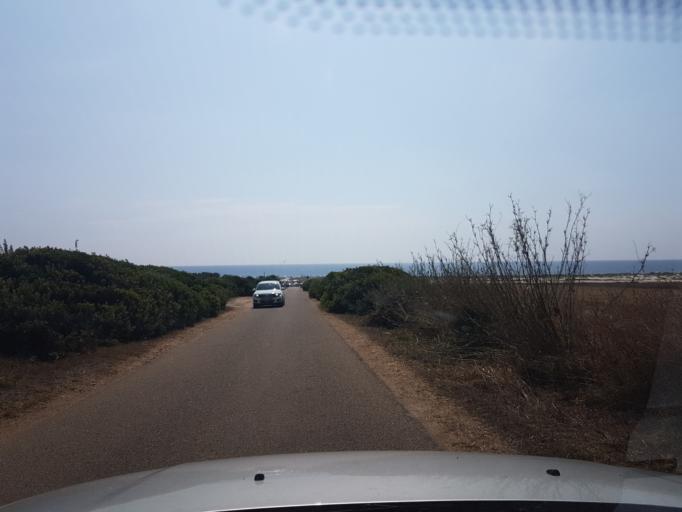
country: IT
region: Sardinia
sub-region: Provincia di Oristano
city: Cabras
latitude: 39.9703
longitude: 8.4031
